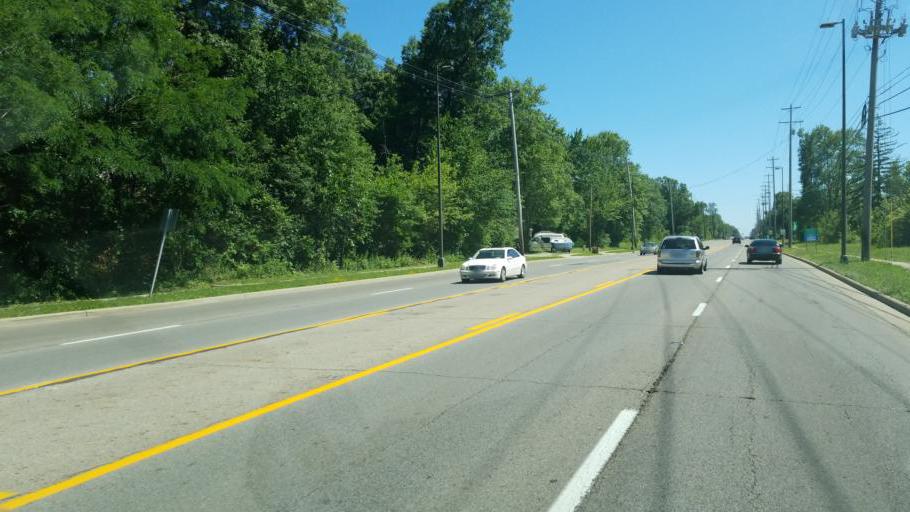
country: US
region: Ohio
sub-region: Franklin County
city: Gahanna
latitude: 40.0281
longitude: -82.9108
